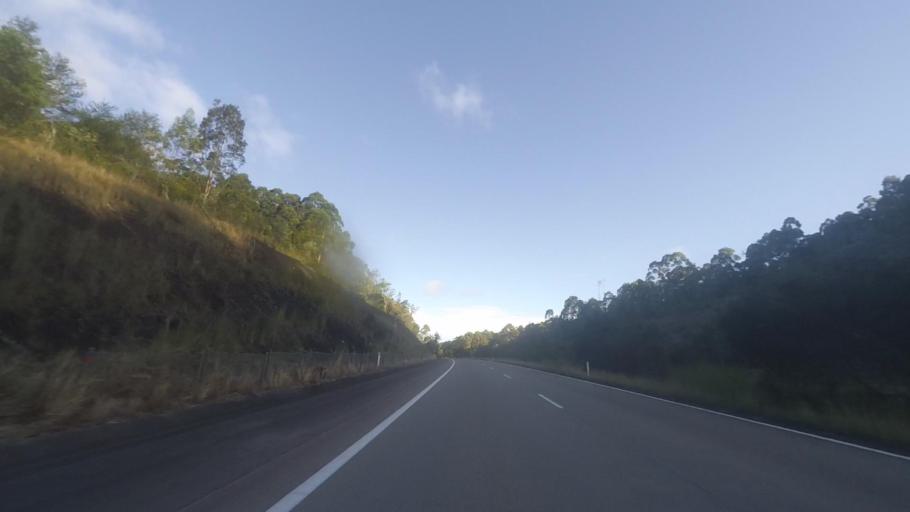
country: AU
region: New South Wales
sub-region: Great Lakes
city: Bulahdelah
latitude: -32.2774
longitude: 152.3306
